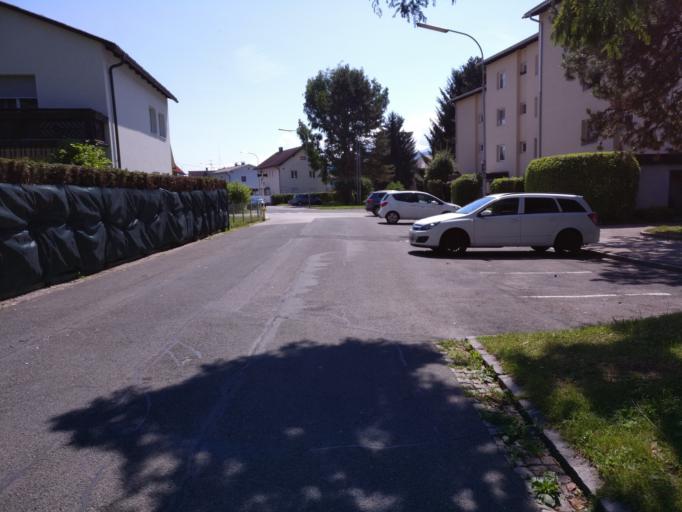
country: AT
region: Carinthia
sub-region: Klagenfurt am Woerthersee
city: Klagenfurt am Woerthersee
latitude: 46.6104
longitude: 14.2838
